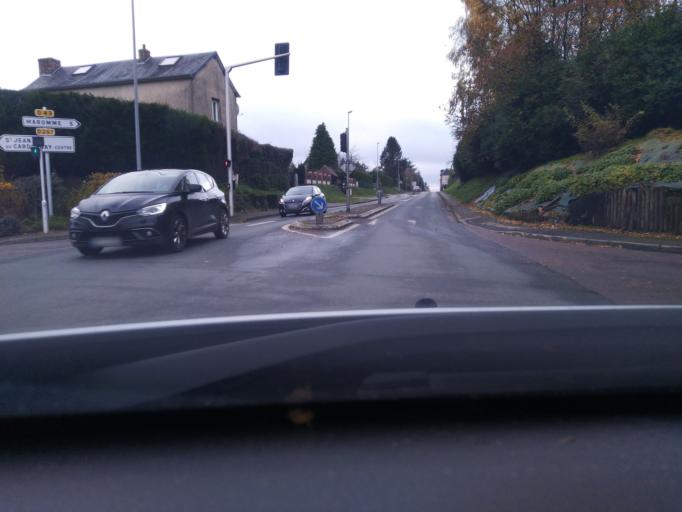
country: FR
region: Haute-Normandie
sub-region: Departement de la Seine-Maritime
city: La Vaupaliere
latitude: 49.4905
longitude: 1.0003
